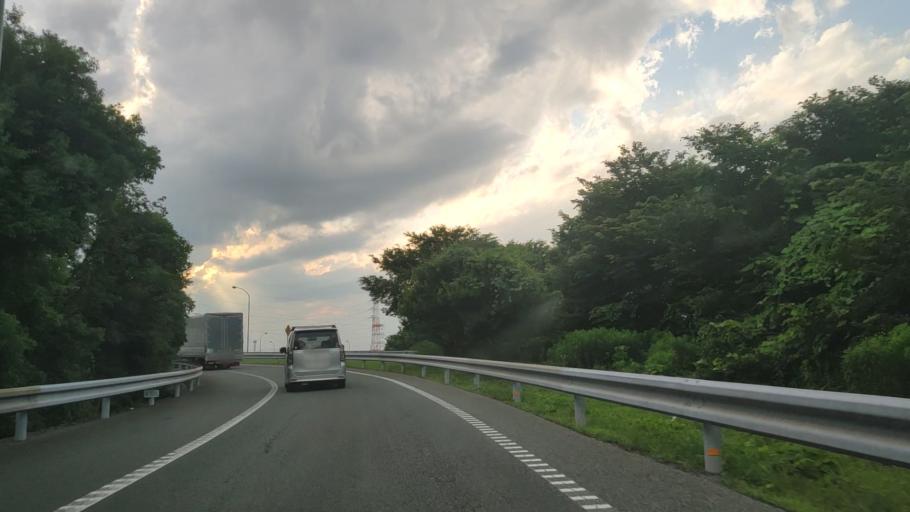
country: JP
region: Saitama
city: Hanno
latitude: 35.7963
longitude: 139.3218
